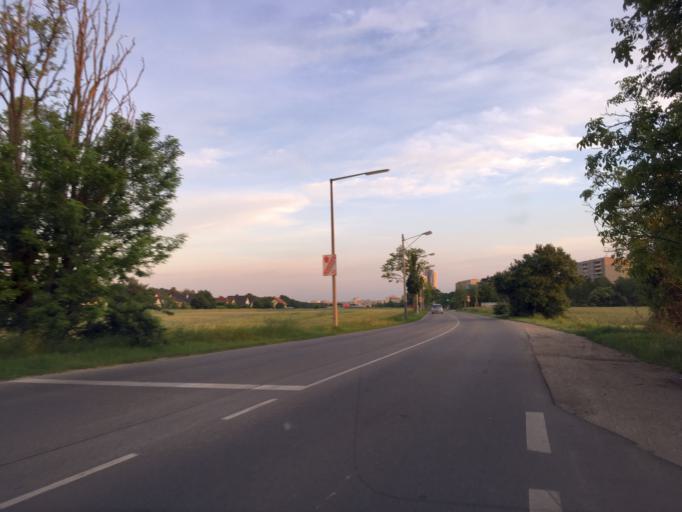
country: AT
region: Lower Austria
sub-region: Politischer Bezirk Wien-Umgebung
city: Gerasdorf bei Wien
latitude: 48.2775
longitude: 16.4590
